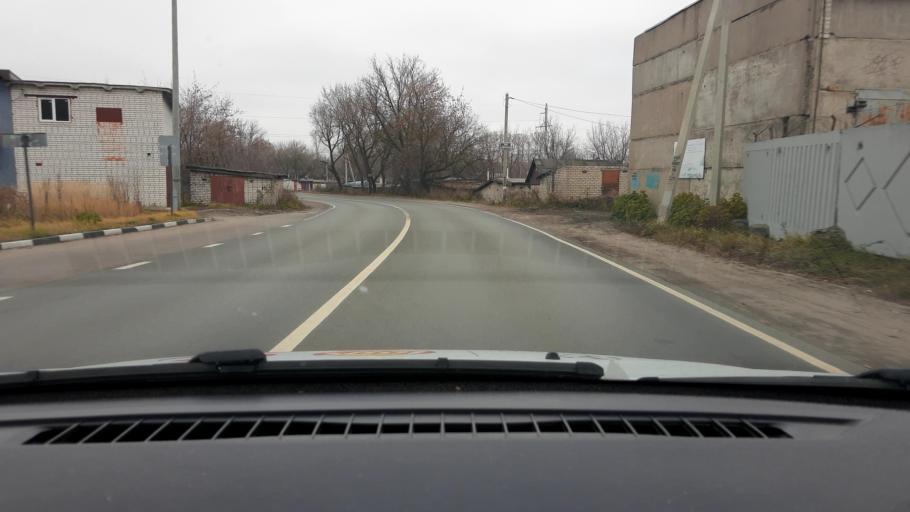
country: RU
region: Nizjnij Novgorod
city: Novaya Balakhna
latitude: 56.5056
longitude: 43.5924
